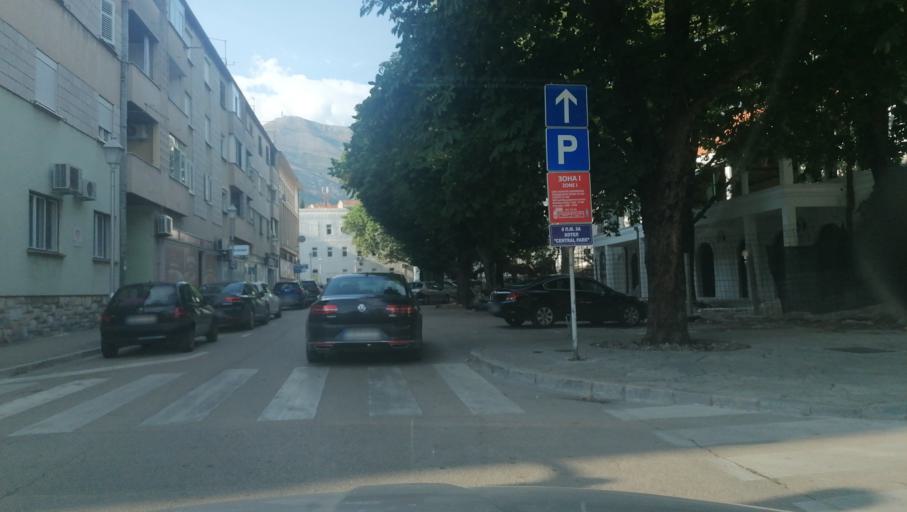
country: BA
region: Republika Srpska
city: Trebinje
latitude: 42.7112
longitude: 18.3439
